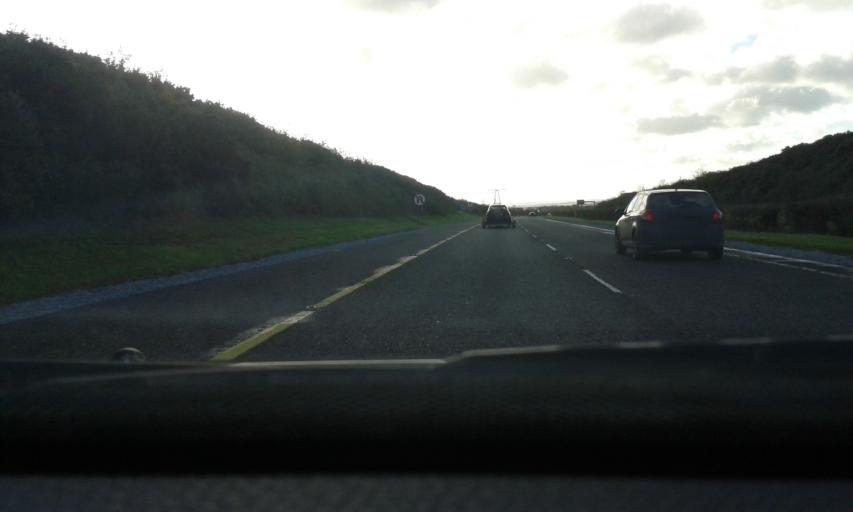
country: IE
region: Munster
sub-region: County Cork
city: Watergrasshill
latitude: 52.0071
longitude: -8.3419
